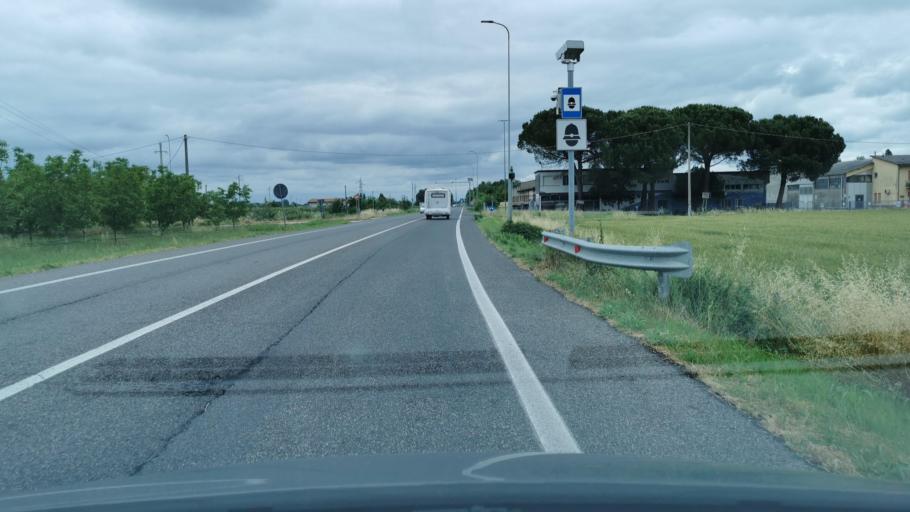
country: IT
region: Emilia-Romagna
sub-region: Provincia di Ravenna
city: Granarolo
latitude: 44.3549
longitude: 11.9281
